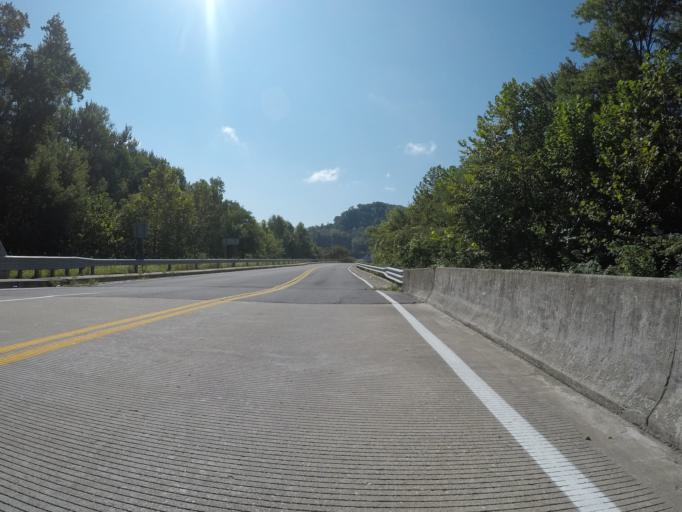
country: US
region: Ohio
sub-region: Lawrence County
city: Burlington
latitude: 38.4047
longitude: -82.4929
